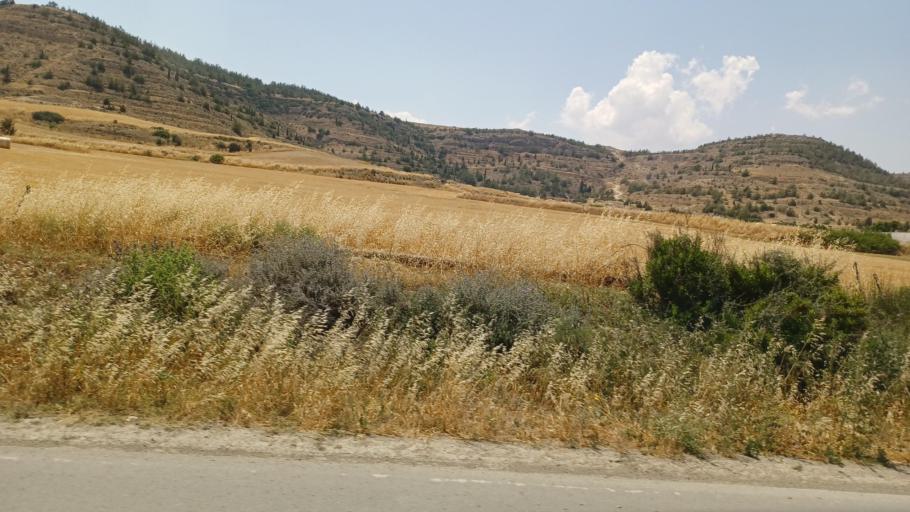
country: CY
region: Larnaka
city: Voroklini
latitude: 34.9947
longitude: 33.6557
